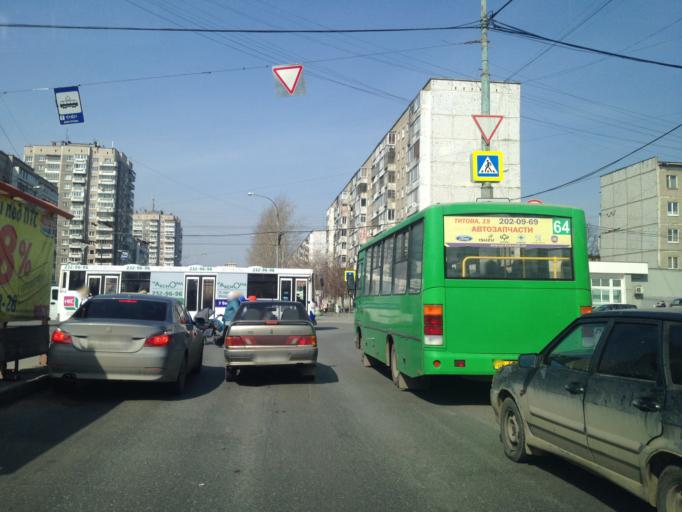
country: RU
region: Sverdlovsk
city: Sovkhoznyy
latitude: 56.8307
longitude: 60.5450
